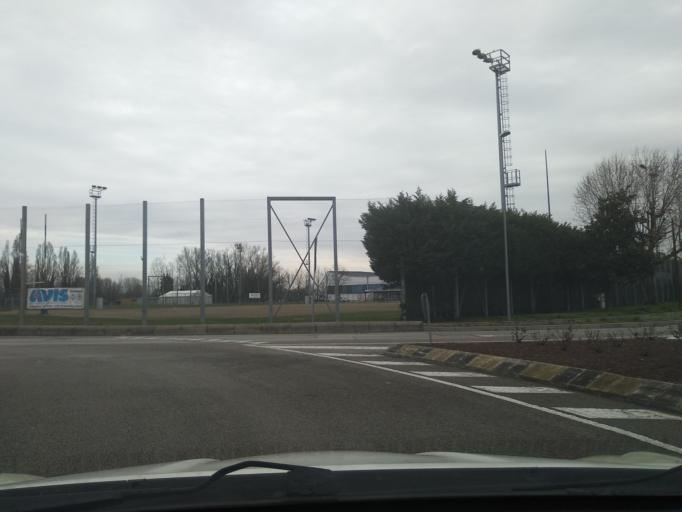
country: IT
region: Veneto
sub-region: Provincia di Padova
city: Selvazzano Dentro
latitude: 45.3894
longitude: 11.7993
